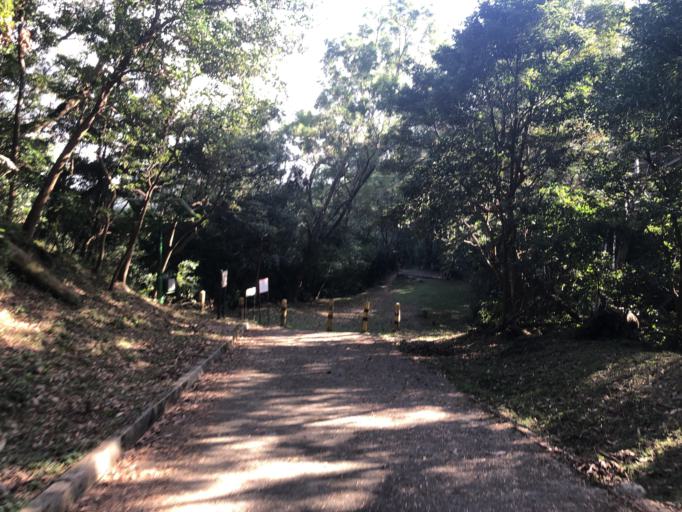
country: HK
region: Tsuen Wan
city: Tsuen Wan
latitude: 22.3886
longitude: 114.0844
